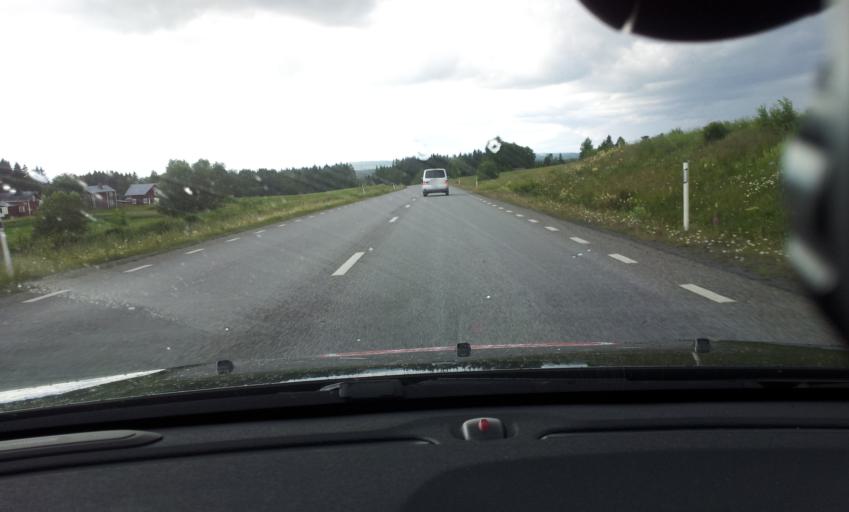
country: SE
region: Jaemtland
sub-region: Krokoms Kommun
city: Valla
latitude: 63.3056
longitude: 13.8749
